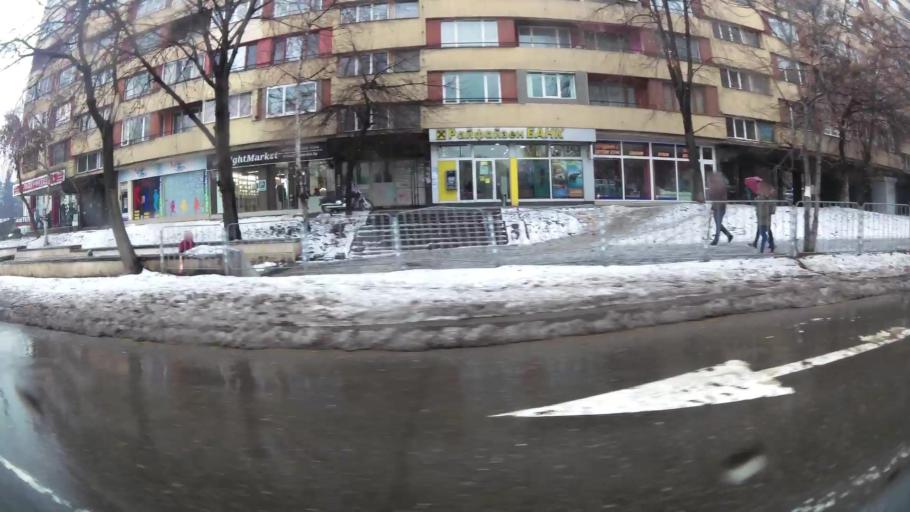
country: BG
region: Sofia-Capital
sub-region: Stolichna Obshtina
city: Sofia
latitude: 42.6723
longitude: 23.2938
